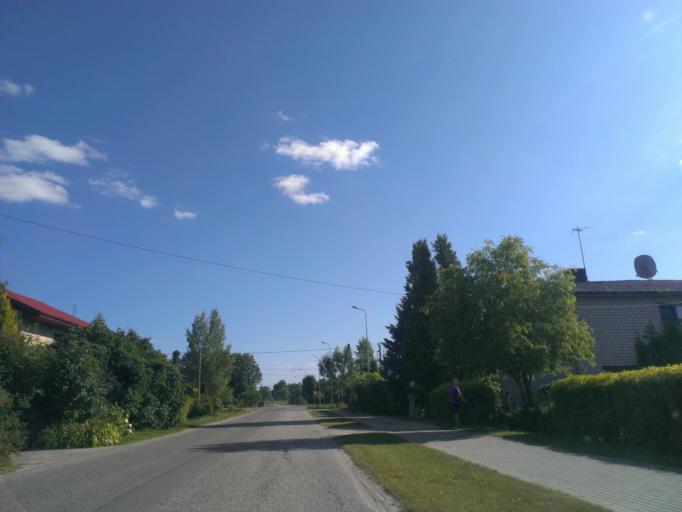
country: LV
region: Sigulda
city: Sigulda
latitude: 57.1602
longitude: 24.8884
